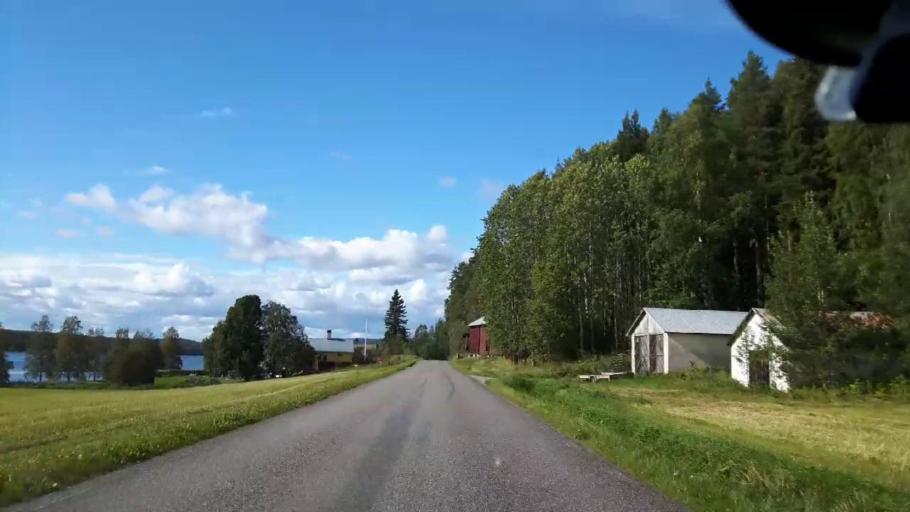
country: SE
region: Jaemtland
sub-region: Braecke Kommun
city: Braecke
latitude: 63.1715
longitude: 15.5708
